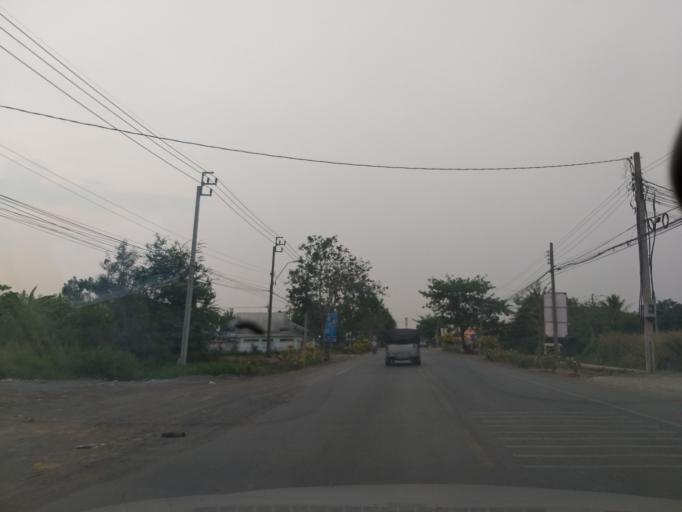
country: TH
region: Bangkok
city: Nong Chok
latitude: 13.8284
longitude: 100.9148
